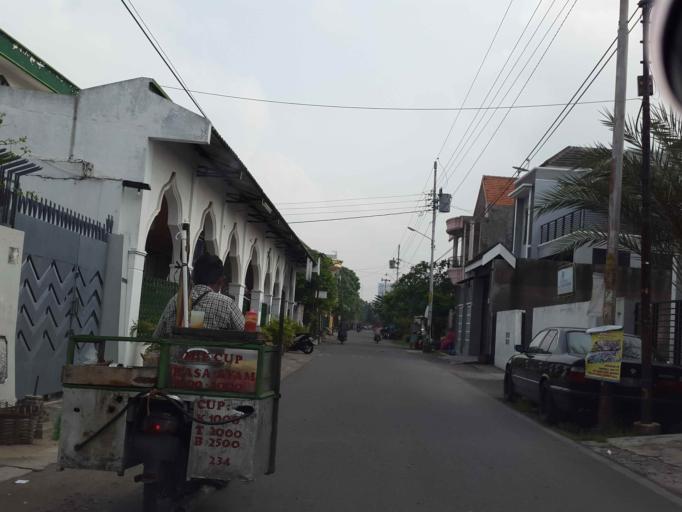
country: ID
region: Central Java
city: Grogol
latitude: -7.5751
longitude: 110.8063
